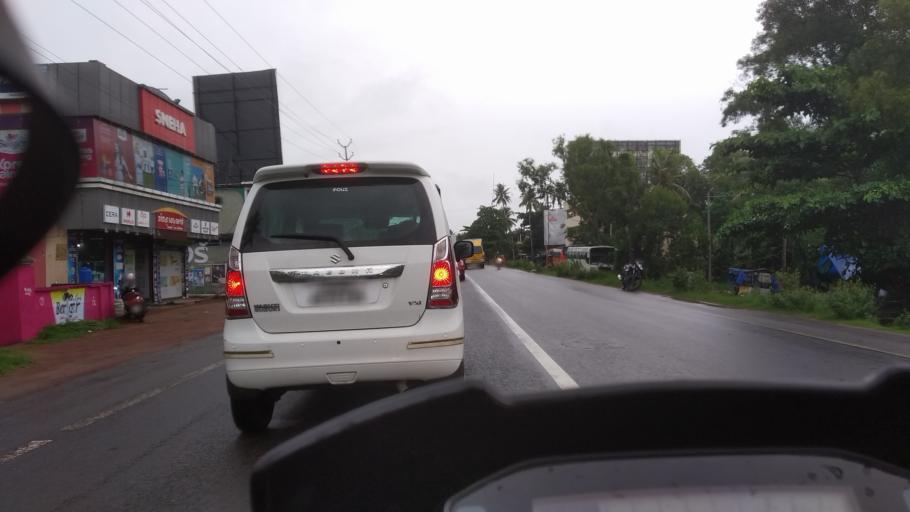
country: IN
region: Kerala
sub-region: Alappuzha
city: Kayankulam
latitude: 9.1246
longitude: 76.5173
